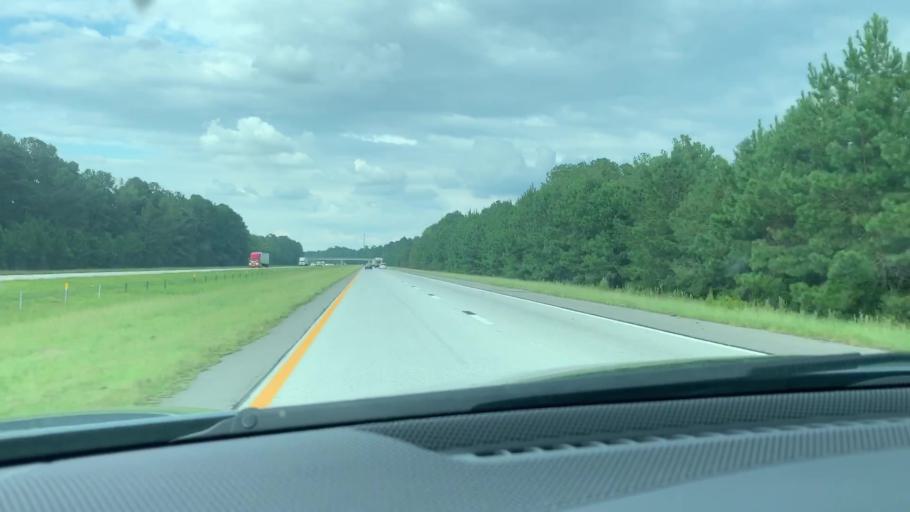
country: US
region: South Carolina
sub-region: Dorchester County
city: Saint George
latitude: 33.2884
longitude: -80.5607
